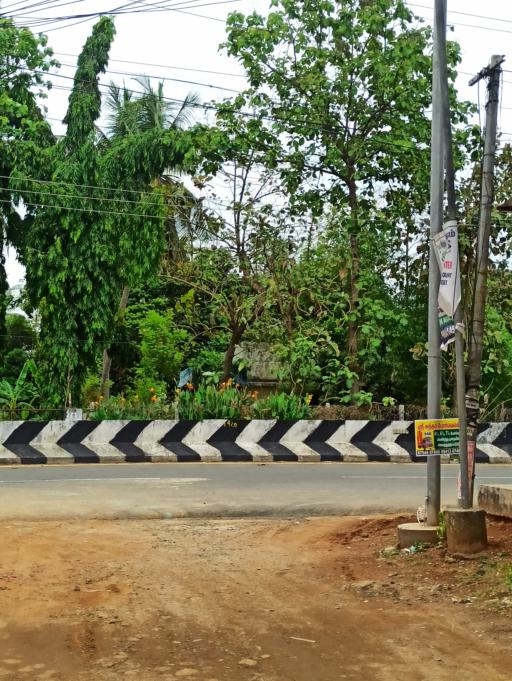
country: IN
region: Tamil Nadu
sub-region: Kancheepuram
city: Vandalur
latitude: 12.8995
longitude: 80.0648
